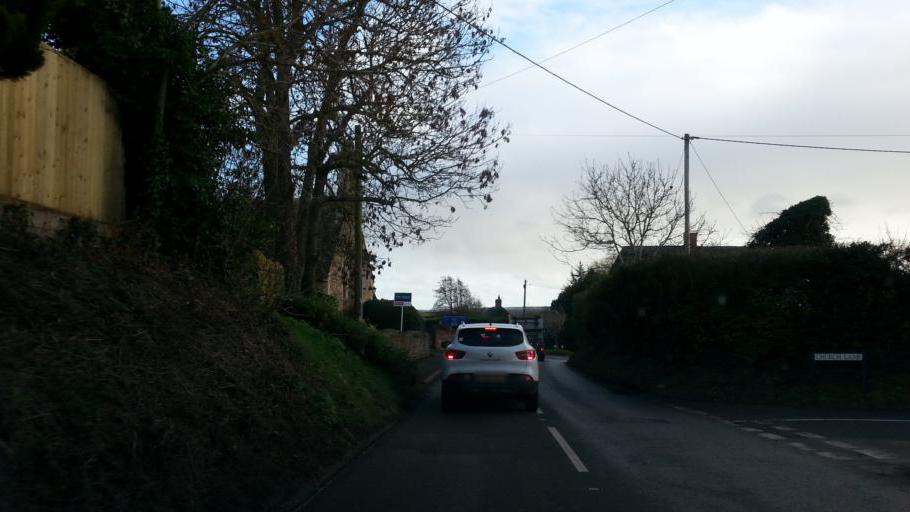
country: GB
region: England
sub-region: Oxfordshire
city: Faringdon
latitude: 51.6254
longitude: -1.5783
